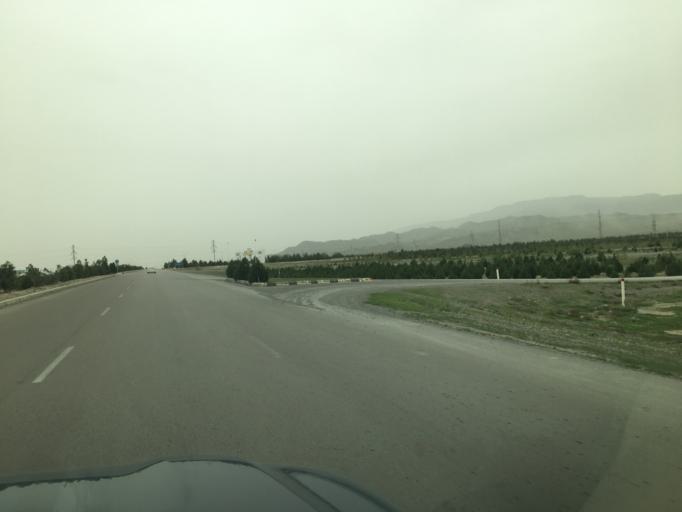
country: TM
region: Ahal
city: Baharly
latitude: 38.2851
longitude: 57.6603
